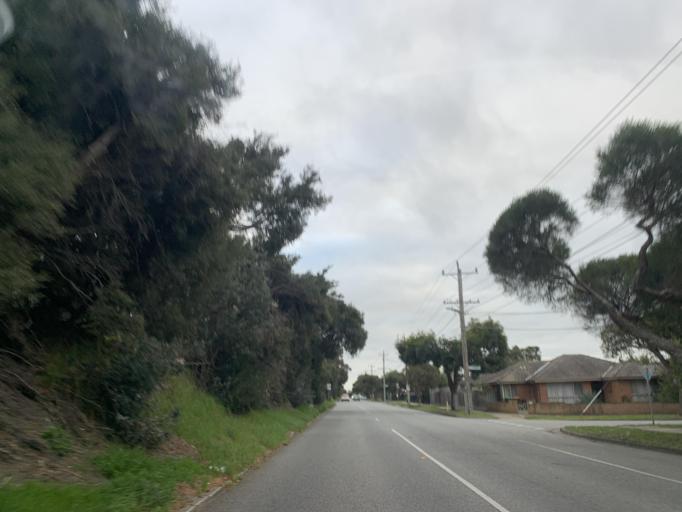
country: AU
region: Victoria
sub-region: Frankston
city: Seaford
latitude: -38.0972
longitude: 145.1284
